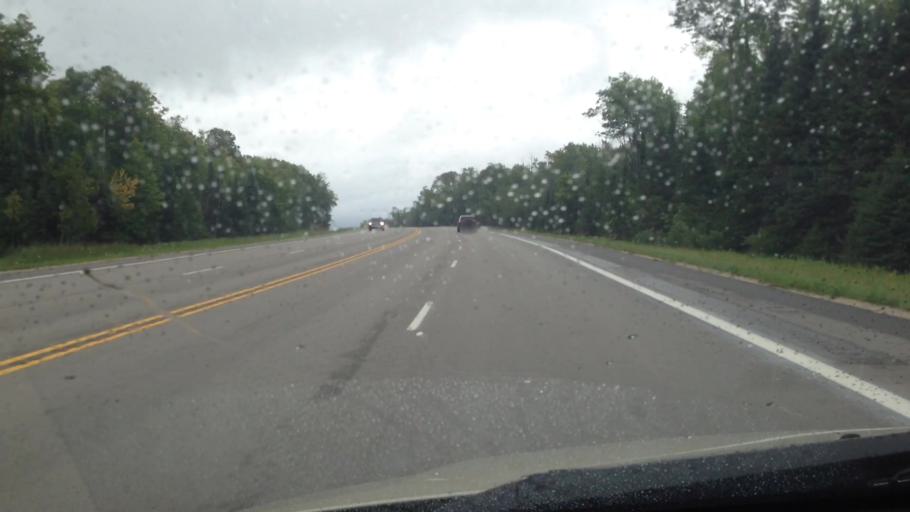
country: US
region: Michigan
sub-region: Schoolcraft County
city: Manistique
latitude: 45.8971
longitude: -86.4999
